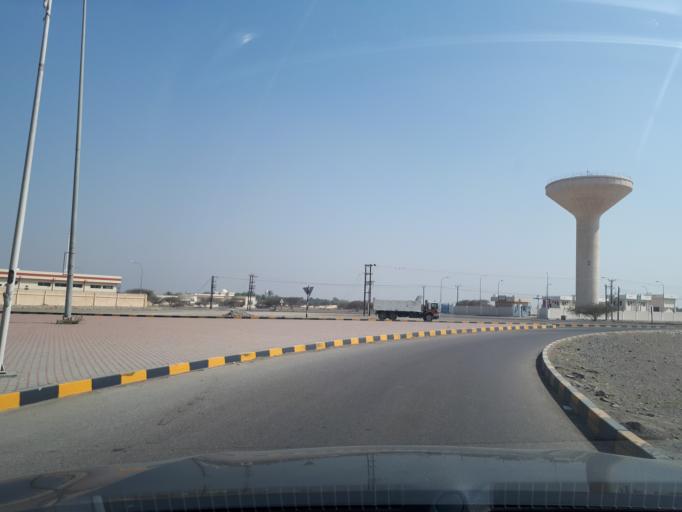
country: OM
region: Al Batinah
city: Shinas
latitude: 24.8583
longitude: 56.3960
